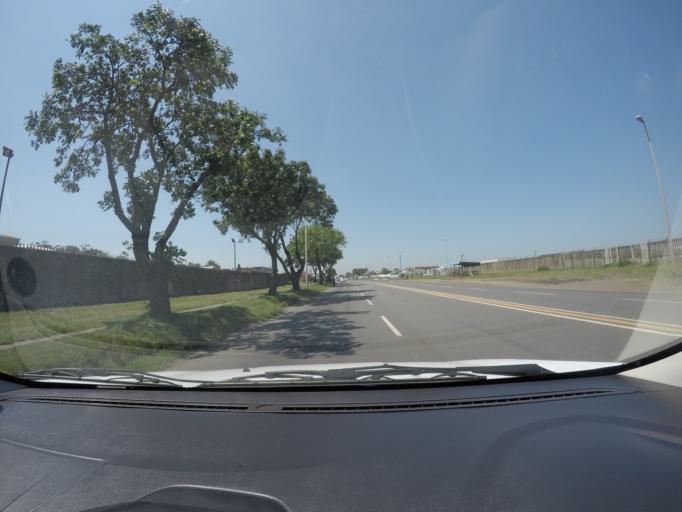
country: ZA
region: KwaZulu-Natal
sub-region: uThungulu District Municipality
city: Richards Bay
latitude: -28.7617
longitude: 32.0222
